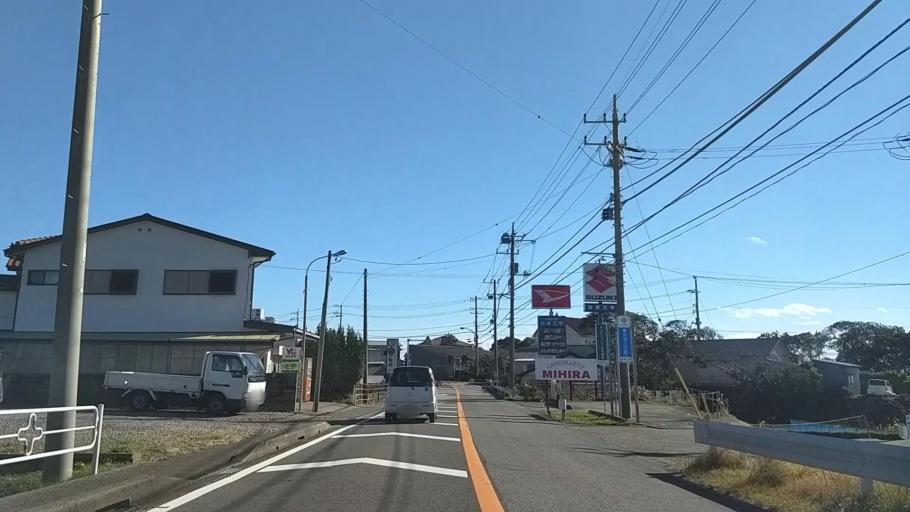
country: JP
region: Chiba
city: Tateyama
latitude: 34.9078
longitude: 139.8905
